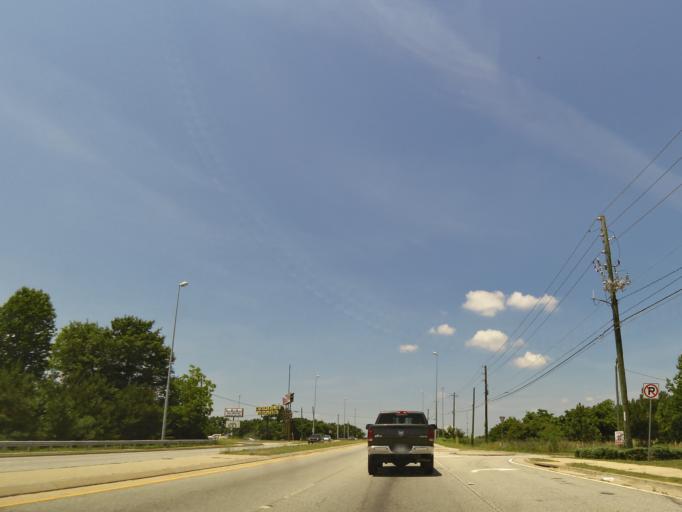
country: US
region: Georgia
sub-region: Bibb County
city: West Point
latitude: 32.8323
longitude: -83.7297
